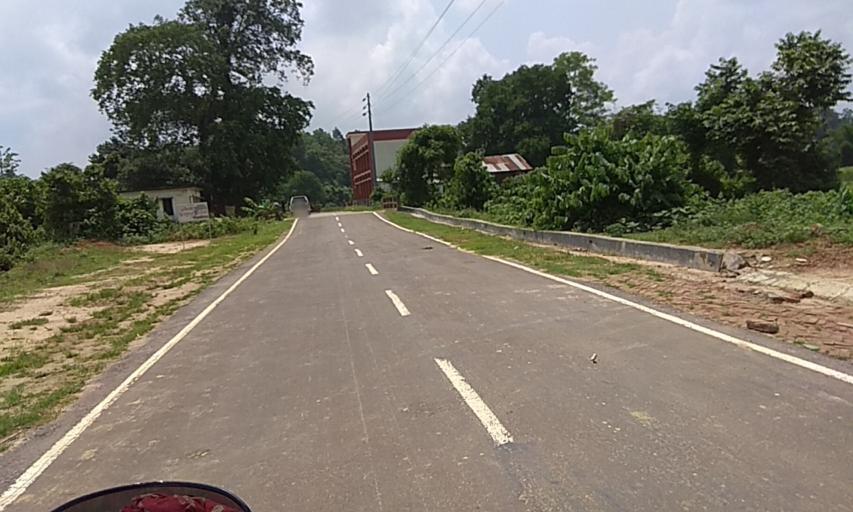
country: BD
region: Chittagong
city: Manikchari
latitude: 22.9356
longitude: 91.9095
